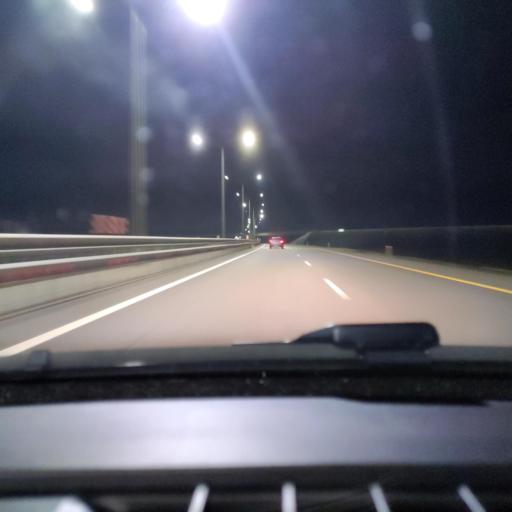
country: RU
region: Voronezj
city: Podkletnoye
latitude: 51.5094
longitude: 39.5150
